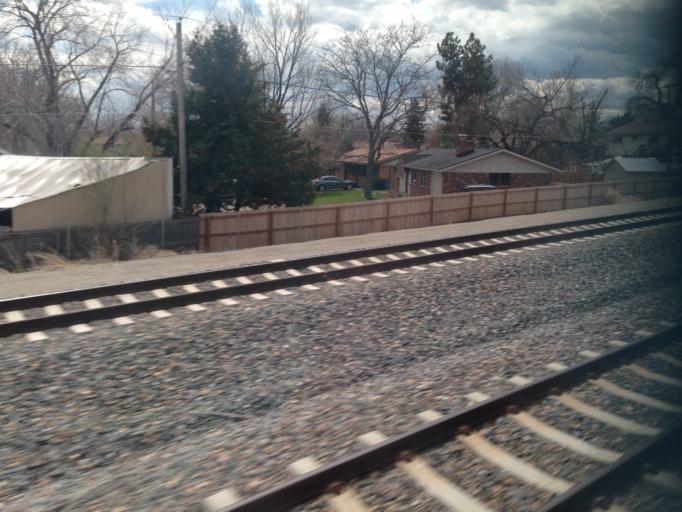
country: US
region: Colorado
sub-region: Jefferson County
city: Arvada
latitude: 39.7945
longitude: -105.0990
